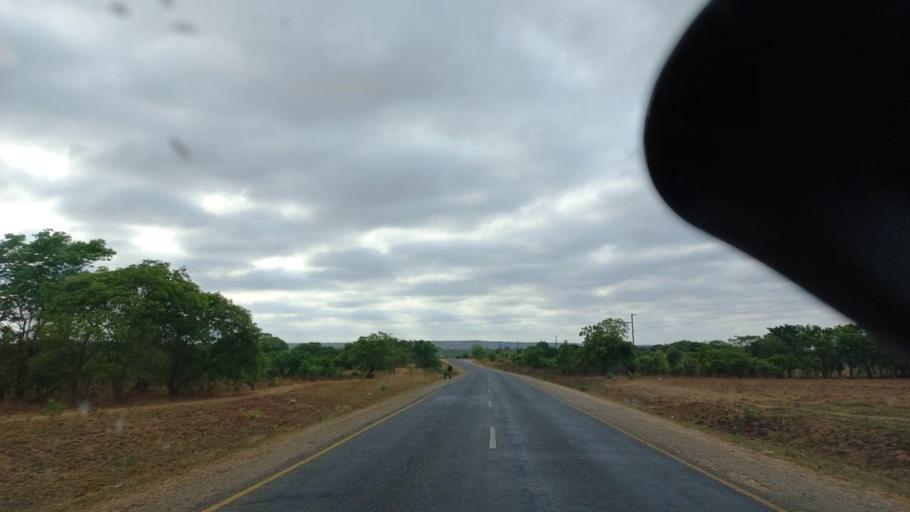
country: ZM
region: Lusaka
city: Chongwe
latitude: -15.2851
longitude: 28.7940
